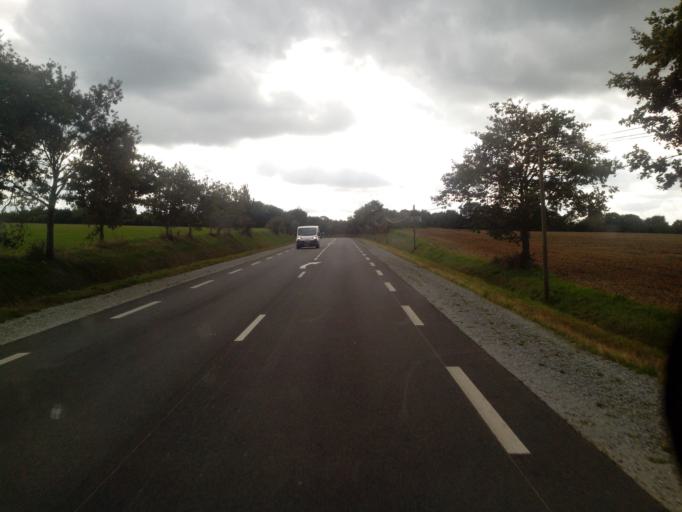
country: FR
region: Brittany
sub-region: Departement du Morbihan
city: Mauron
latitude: 48.0544
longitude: -2.2977
